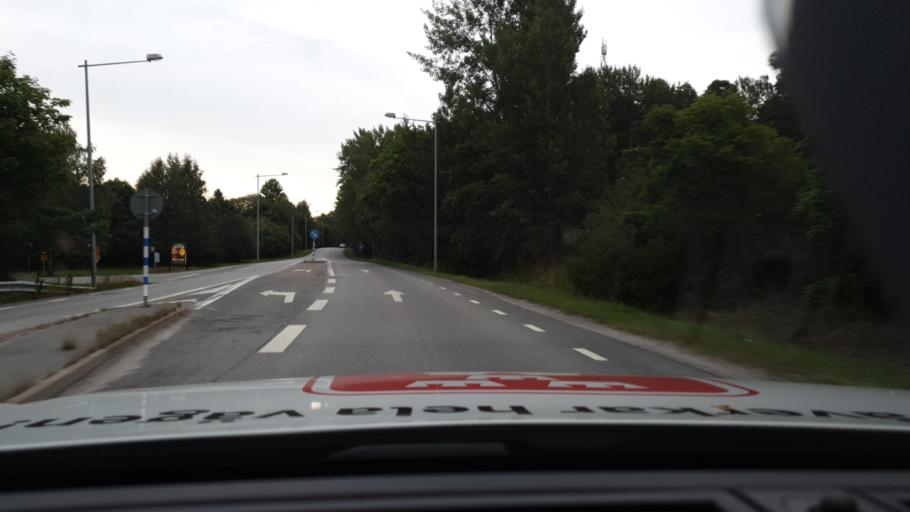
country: SE
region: Stockholm
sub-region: Osterakers Kommun
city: Akersberga
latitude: 59.4819
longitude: 18.3136
